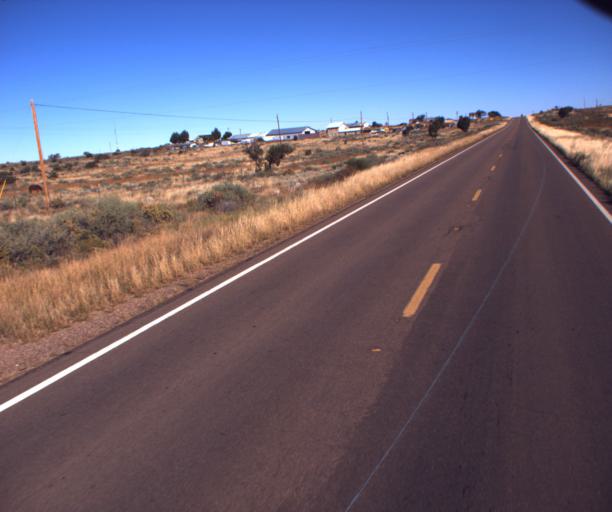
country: US
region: Arizona
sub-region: Navajo County
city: Snowflake
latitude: 34.5573
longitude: -110.0810
